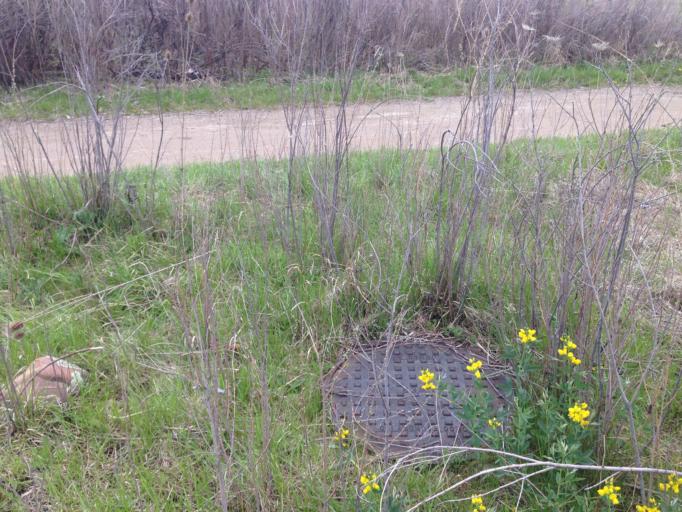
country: US
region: Colorado
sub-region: Boulder County
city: Superior
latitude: 39.9791
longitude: -105.2222
